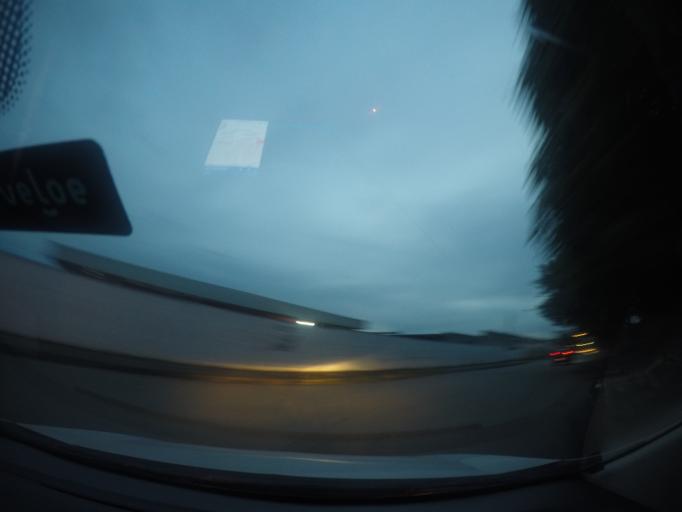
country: BR
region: Goias
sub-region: Goiania
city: Goiania
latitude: -16.6449
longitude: -49.2401
